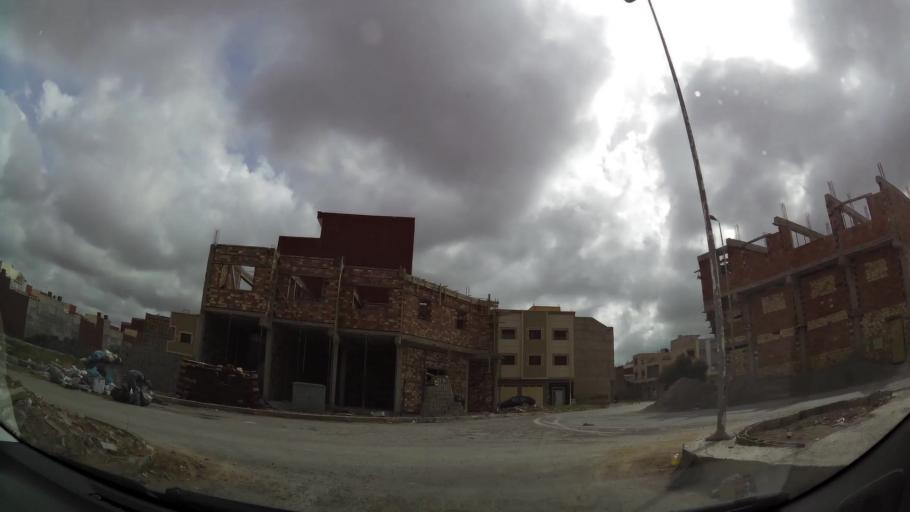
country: MA
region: Oriental
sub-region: Nador
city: Nador
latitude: 35.1652
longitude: -2.9350
